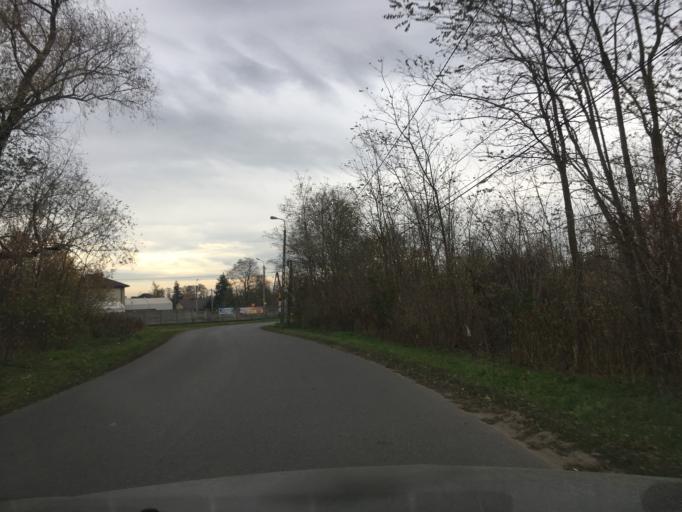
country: PL
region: Masovian Voivodeship
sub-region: Powiat piaseczynski
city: Piaseczno
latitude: 52.0465
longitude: 20.9763
